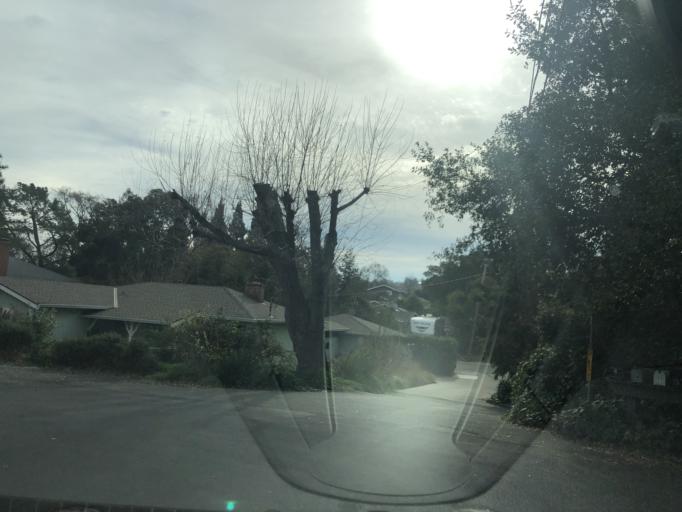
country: US
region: California
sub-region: Contra Costa County
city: Saranap
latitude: 37.8932
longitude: -122.0740
